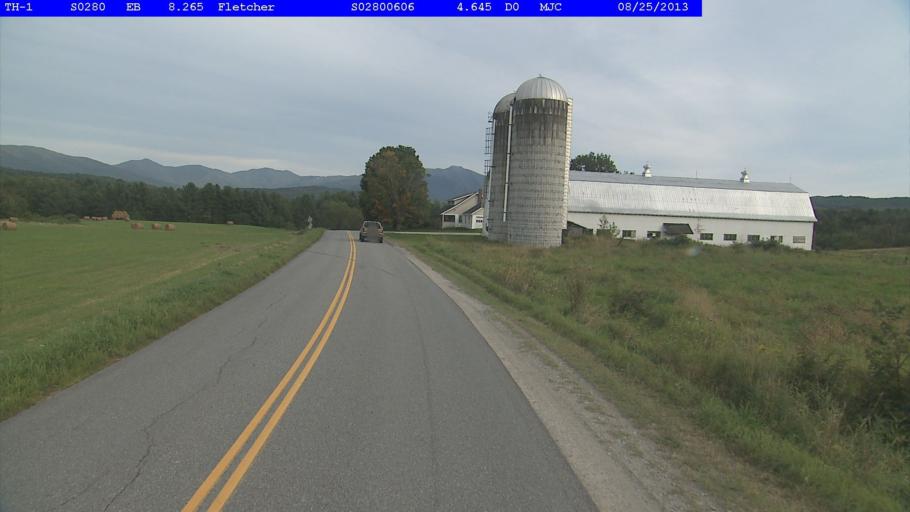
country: US
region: Vermont
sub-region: Chittenden County
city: Jericho
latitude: 44.6652
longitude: -72.8900
